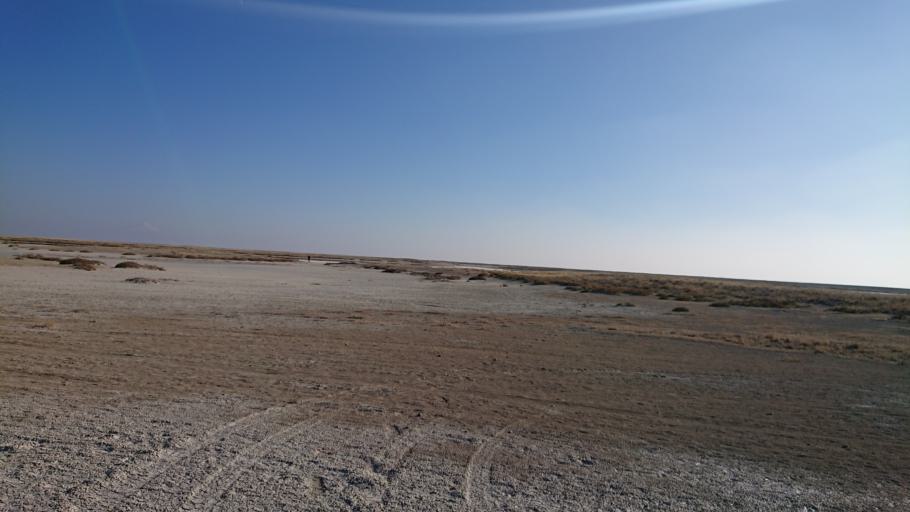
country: TR
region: Aksaray
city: Eskil
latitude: 38.4300
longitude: 33.5067
